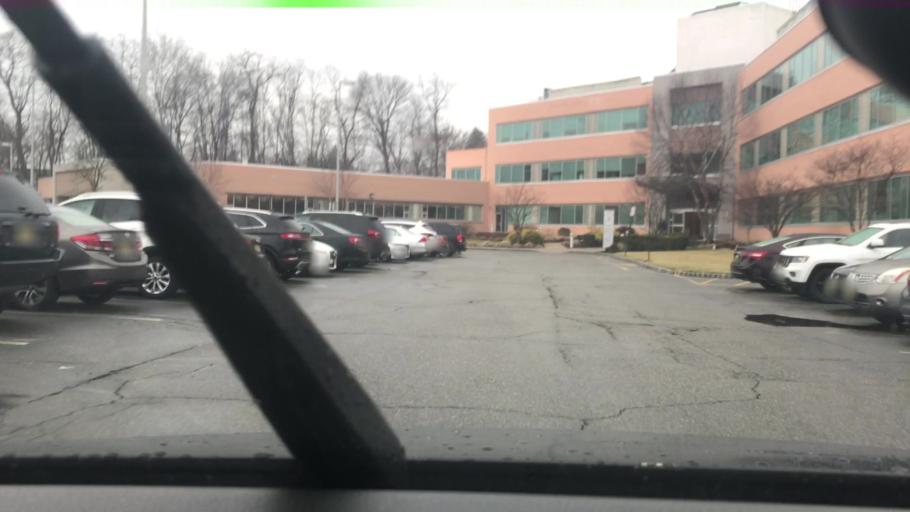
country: US
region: New Jersey
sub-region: Morris County
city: Morris Plains
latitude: 40.8125
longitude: -74.4544
